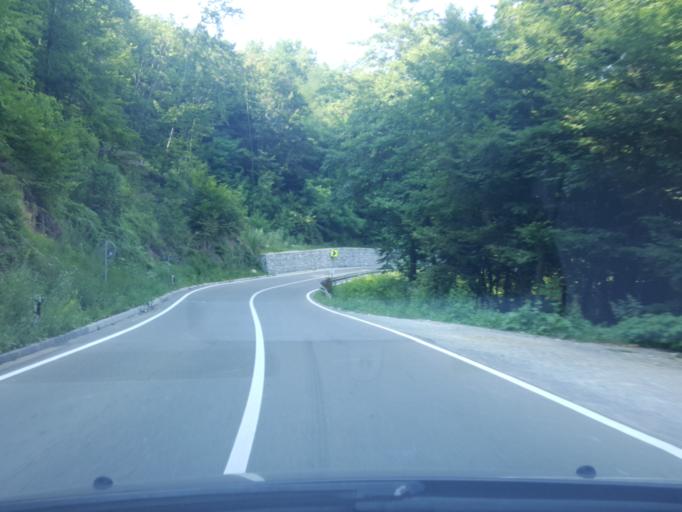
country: RS
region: Central Serbia
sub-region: Moravicki Okrug
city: Gornji Milanovac
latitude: 44.1475
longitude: 20.5014
